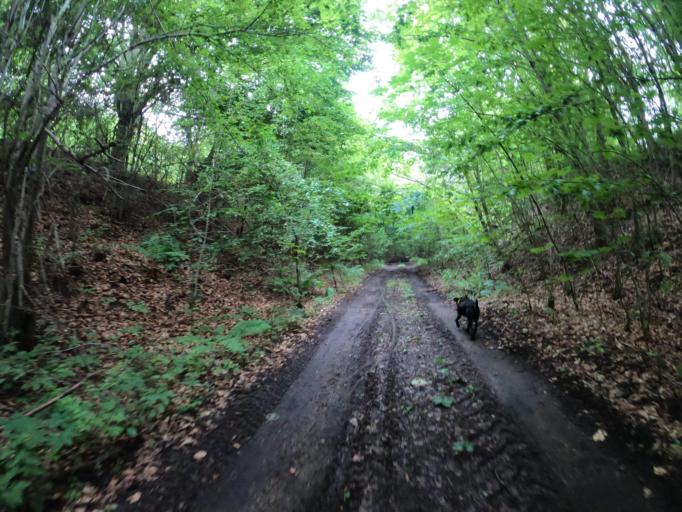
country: PL
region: West Pomeranian Voivodeship
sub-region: Powiat szczecinecki
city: Grzmiaca
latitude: 53.8873
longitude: 16.4847
